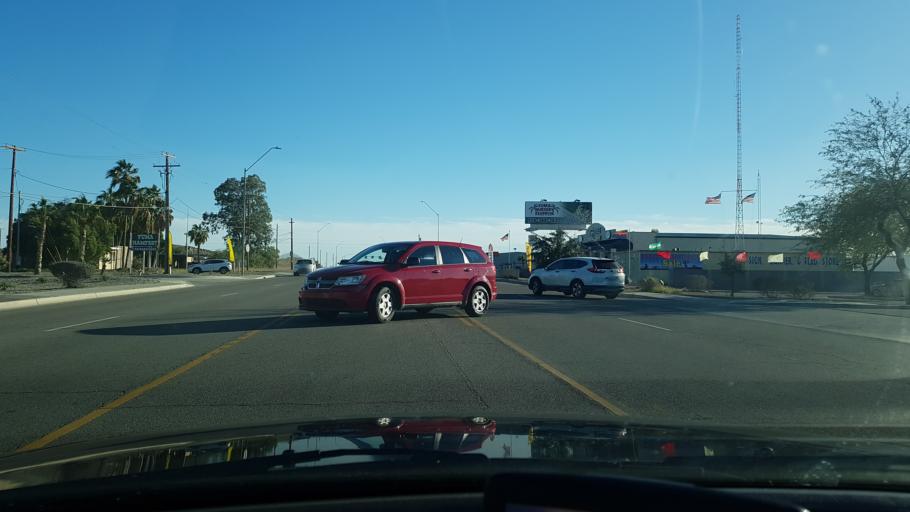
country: US
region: Arizona
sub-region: Yuma County
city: Yuma
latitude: 32.6738
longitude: -114.5988
